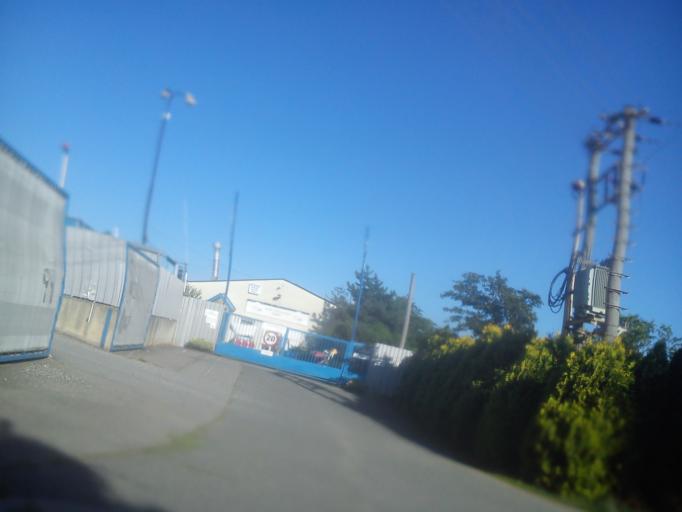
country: CZ
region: South Moravian
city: Sokolnice
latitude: 49.1064
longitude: 16.7376
